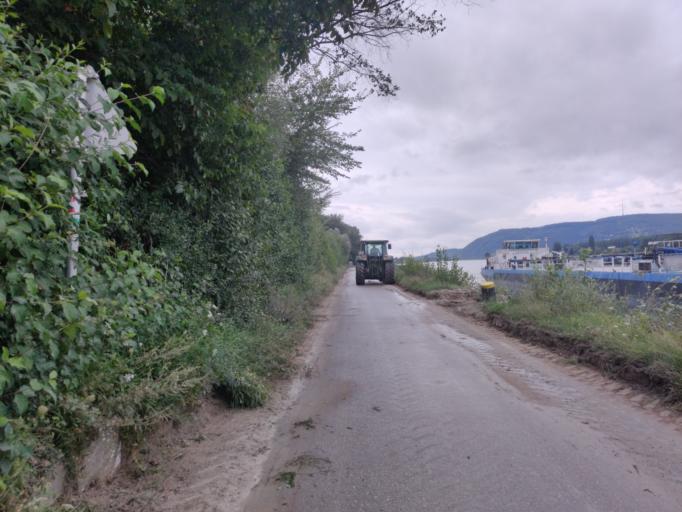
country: AT
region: Lower Austria
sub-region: Politischer Bezirk Korneuburg
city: Bisamberg
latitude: 48.3226
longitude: 16.3375
